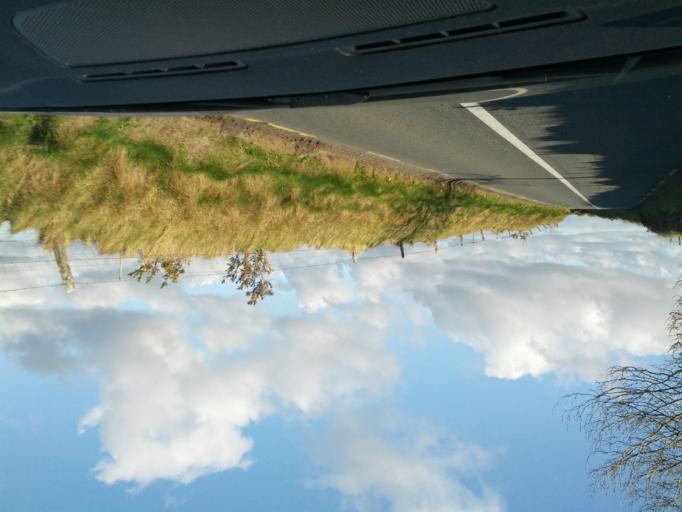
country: IE
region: Connaught
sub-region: Roscommon
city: Castlerea
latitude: 53.5637
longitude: -8.5714
